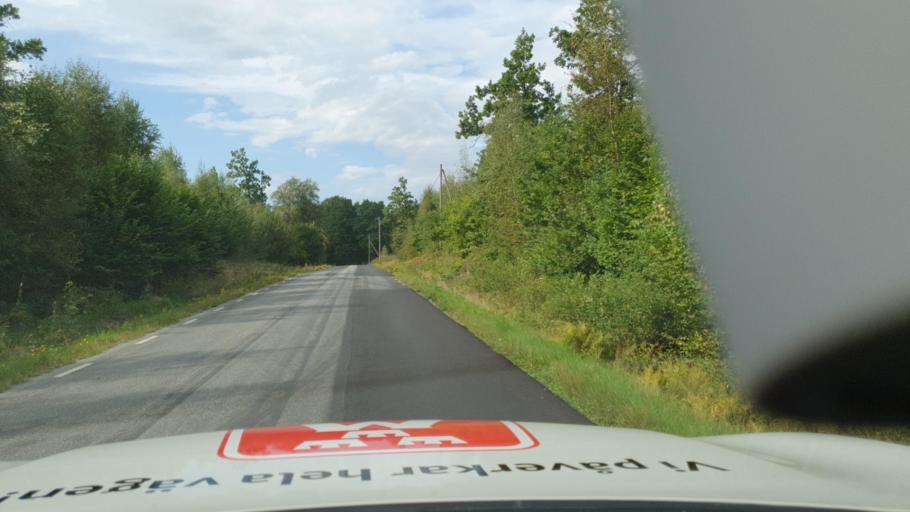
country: SE
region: Vaestra Goetaland
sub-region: Marks Kommun
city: Kinna
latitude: 57.3852
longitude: 12.7290
